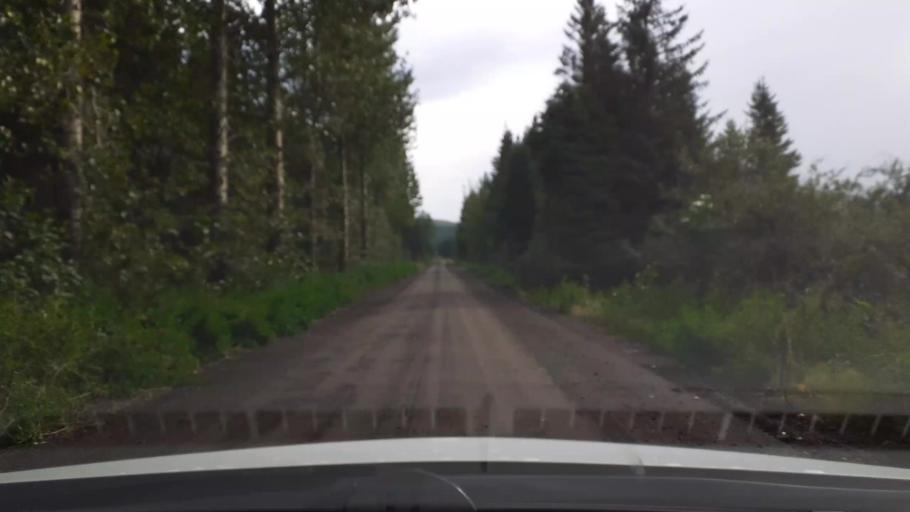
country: IS
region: Capital Region
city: Mosfellsbaer
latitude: 64.5212
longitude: -21.4570
